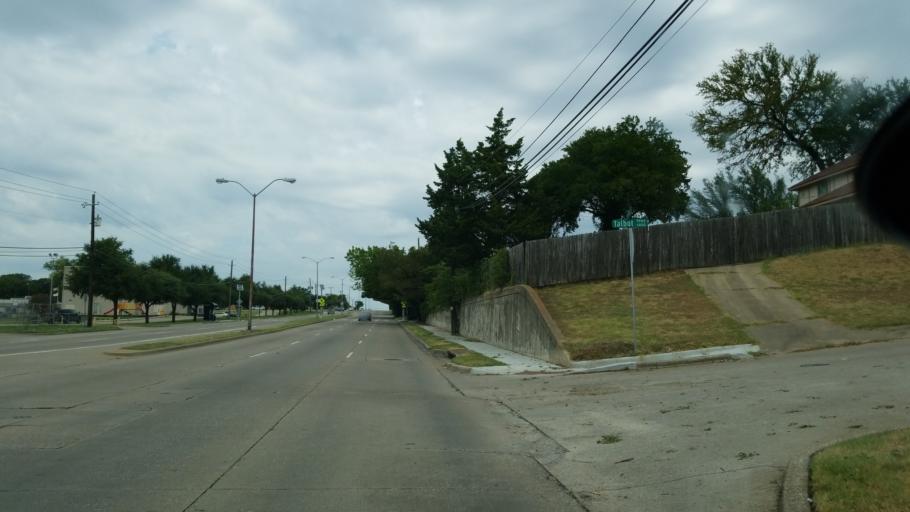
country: US
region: Texas
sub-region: Dallas County
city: Duncanville
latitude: 32.6643
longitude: -96.8570
